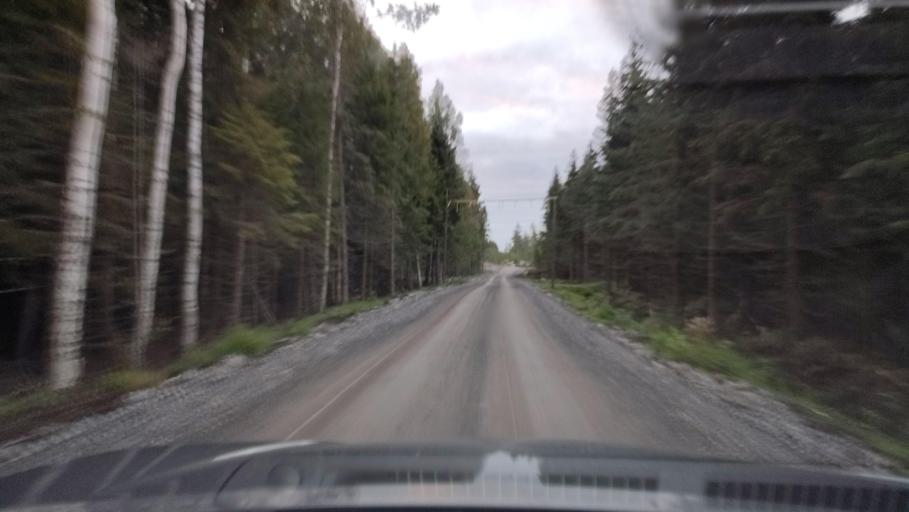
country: FI
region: Ostrobothnia
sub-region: Sydosterbotten
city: Kristinestad
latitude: 62.1902
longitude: 21.5342
